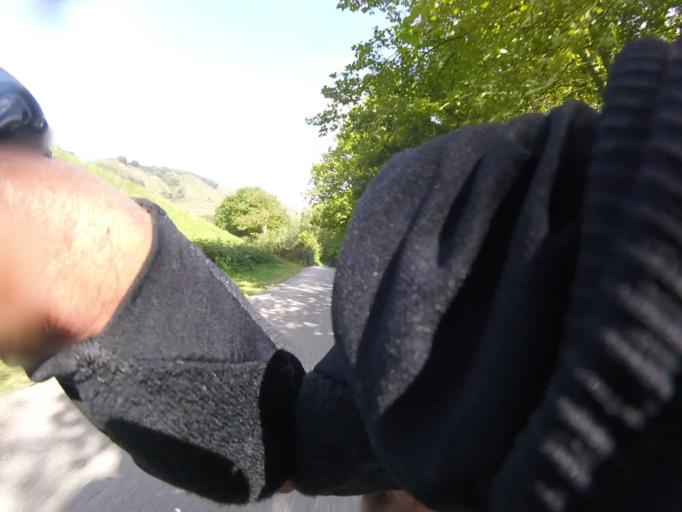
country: ES
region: Navarre
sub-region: Provincia de Navarra
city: Igantzi
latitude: 43.2241
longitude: -1.6760
